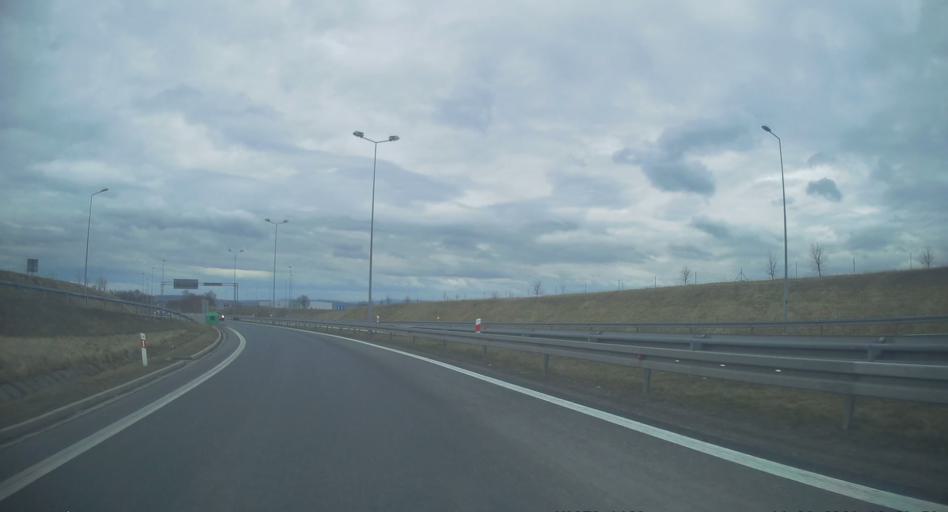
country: PL
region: Lesser Poland Voivodeship
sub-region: Powiat wielicki
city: Szarow
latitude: 49.9892
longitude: 20.2789
